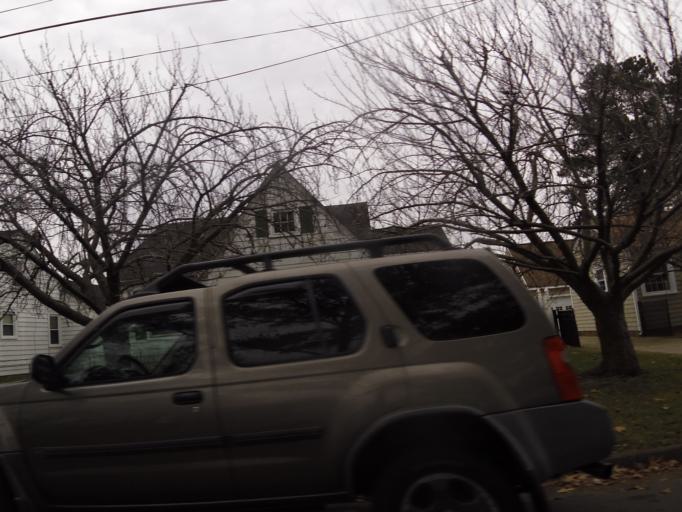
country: US
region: Virginia
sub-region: City of Portsmouth
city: Portsmouth
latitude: 36.8447
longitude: -76.3251
